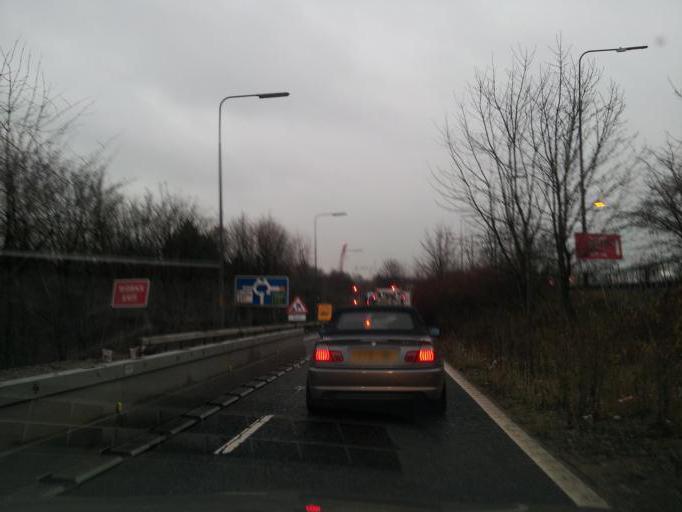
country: GB
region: England
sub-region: Manchester
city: Swinton
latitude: 53.4780
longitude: -2.3742
